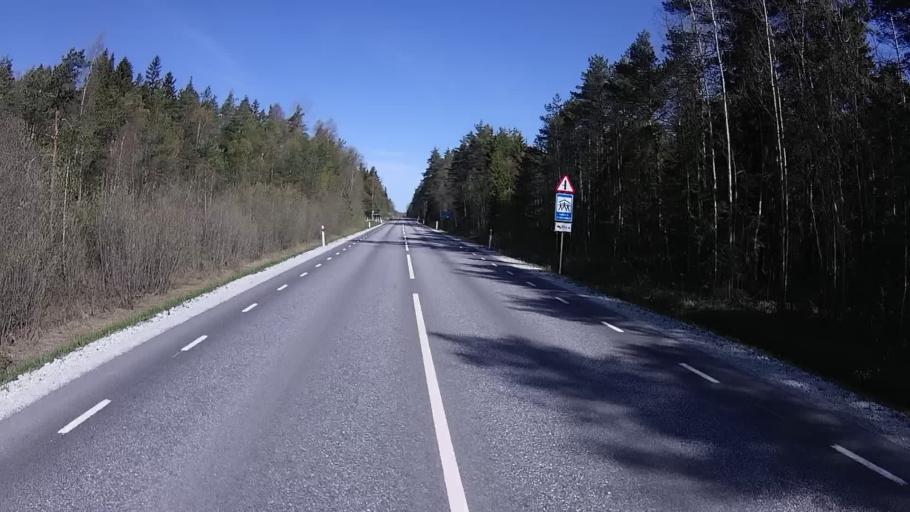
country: EE
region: Raplamaa
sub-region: Jaervakandi vald
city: Jarvakandi
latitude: 58.8588
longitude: 24.7899
